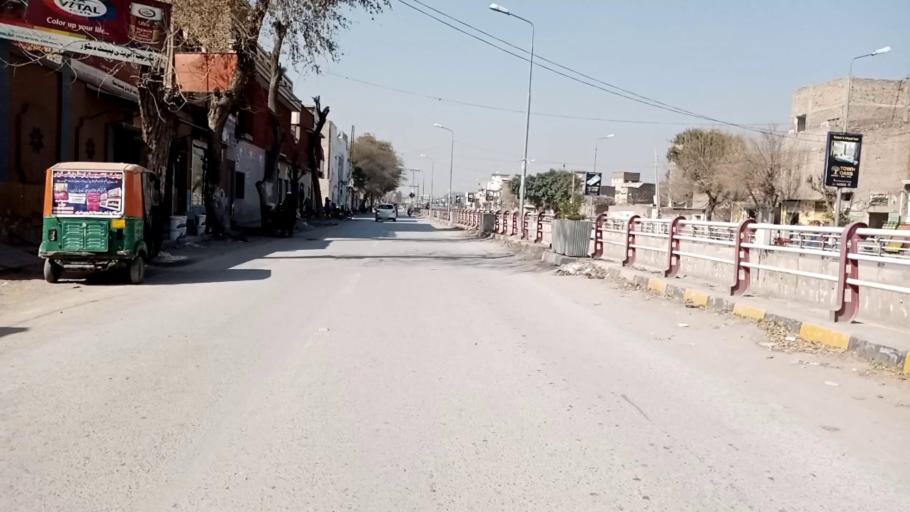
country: PK
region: Khyber Pakhtunkhwa
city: Peshawar
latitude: 33.9785
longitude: 71.5106
